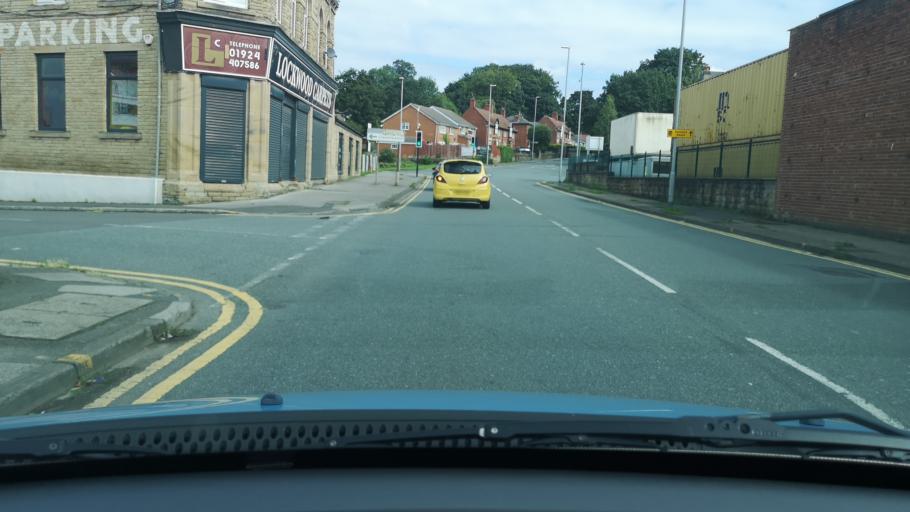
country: GB
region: England
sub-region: Kirklees
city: Liversedge
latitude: 53.7097
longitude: -1.6871
